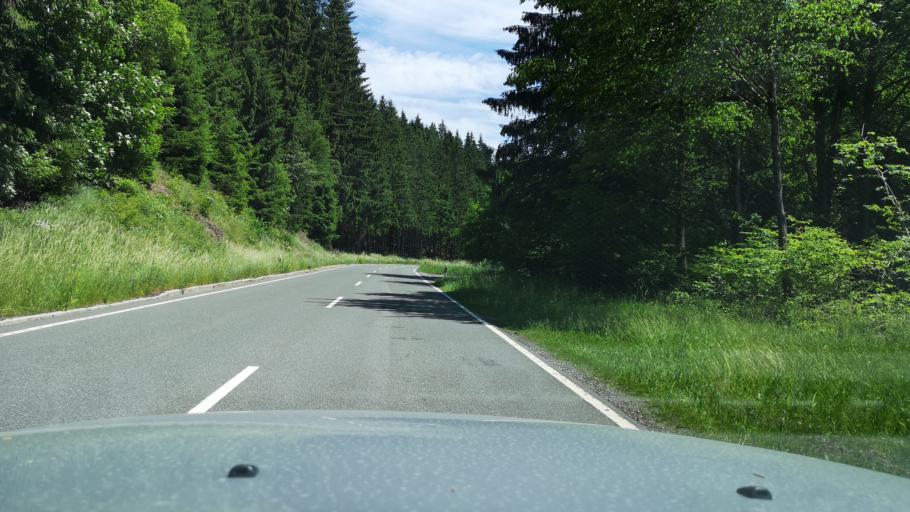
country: DE
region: Bavaria
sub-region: Upper Franconia
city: Tschirn
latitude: 50.3957
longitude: 11.4391
